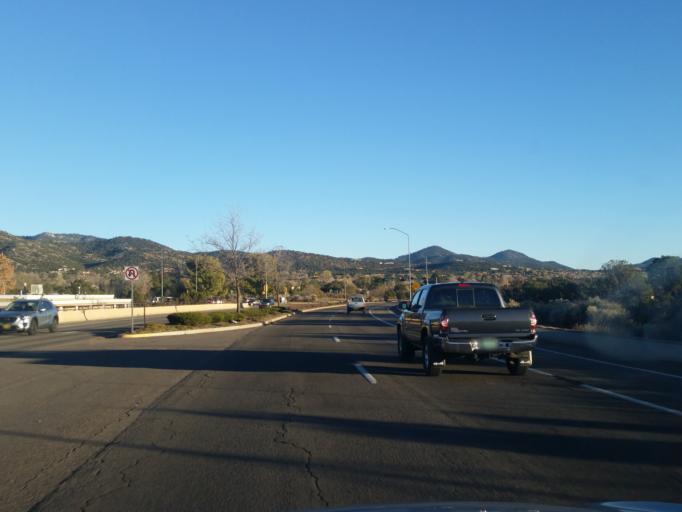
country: US
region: New Mexico
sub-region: Santa Fe County
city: Santa Fe
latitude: 35.6554
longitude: -105.9404
